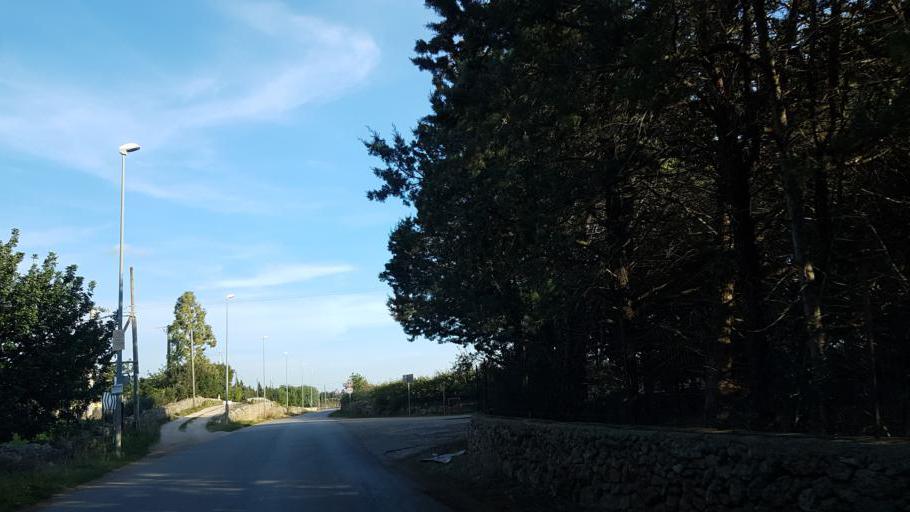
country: IT
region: Apulia
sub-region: Provincia di Brindisi
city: San Vito dei Normanni
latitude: 40.7046
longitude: 17.7140
